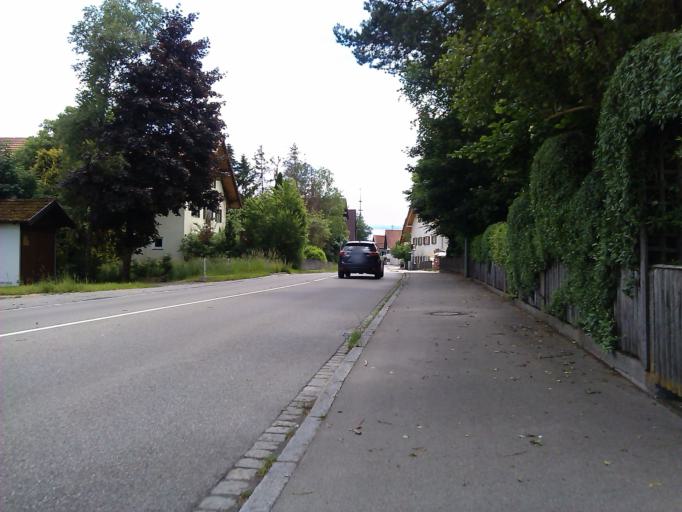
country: DE
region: Bavaria
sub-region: Swabia
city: Biessenhofen
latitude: 47.8354
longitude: 10.6402
